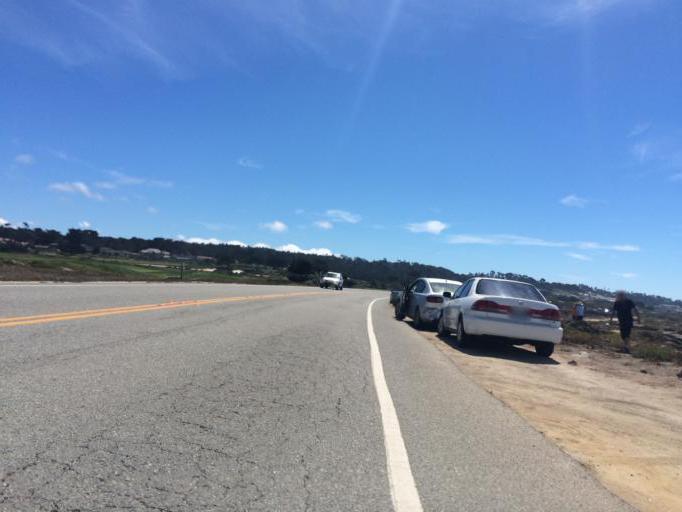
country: US
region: California
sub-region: Monterey County
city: Del Monte Forest
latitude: 36.5967
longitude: -121.9609
